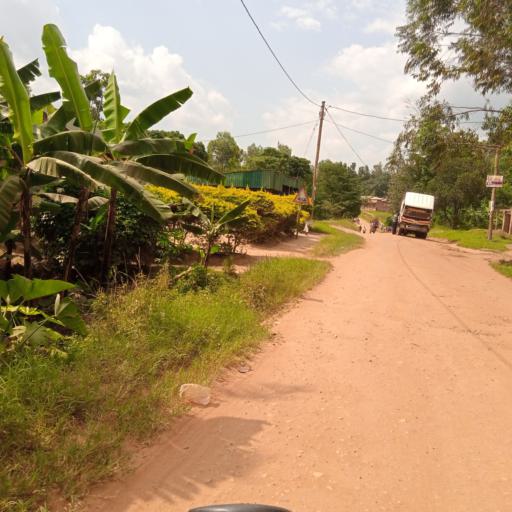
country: UG
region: Eastern Region
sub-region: Mbale District
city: Mbale
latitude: 1.1070
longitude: 34.2002
